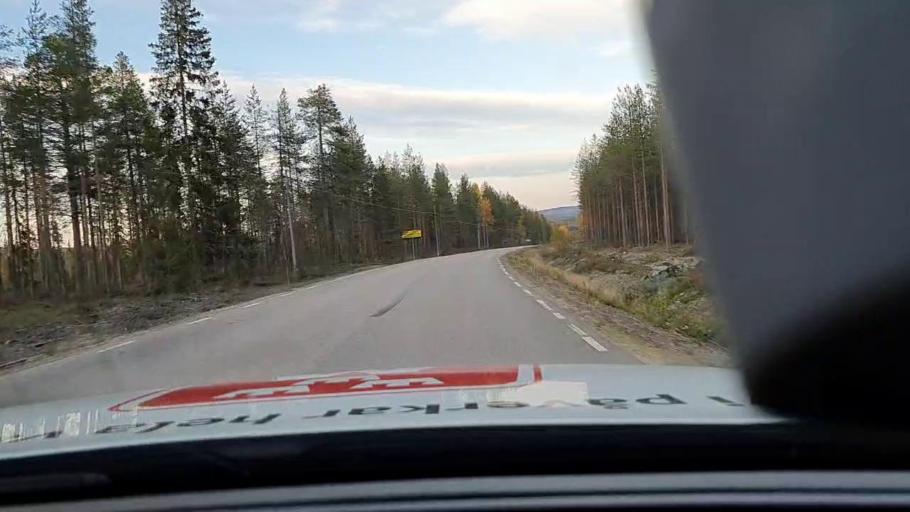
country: SE
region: Norrbotten
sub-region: Overkalix Kommun
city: OEverkalix
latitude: 66.3299
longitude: 22.7782
